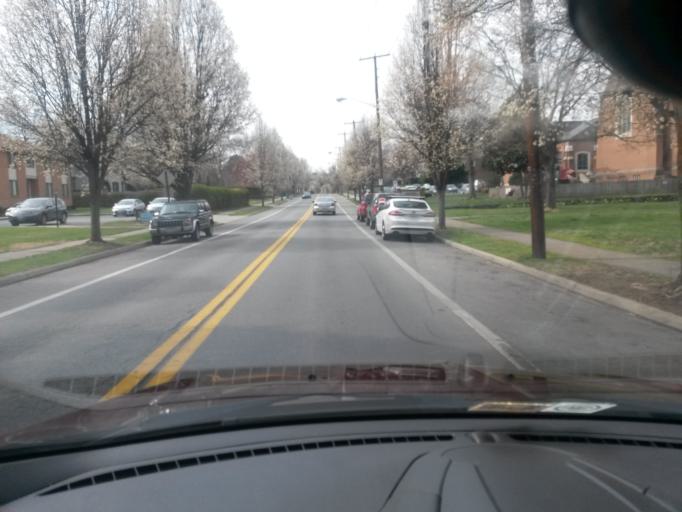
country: US
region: Virginia
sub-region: City of Roanoke
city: Roanoke
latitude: 37.2606
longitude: -79.9800
